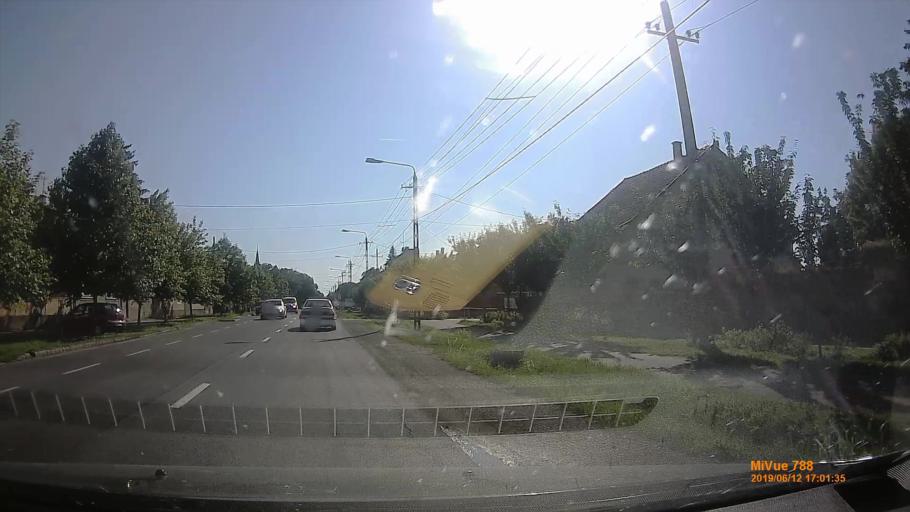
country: HU
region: Csongrad
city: Deszk
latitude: 46.2189
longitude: 20.2399
